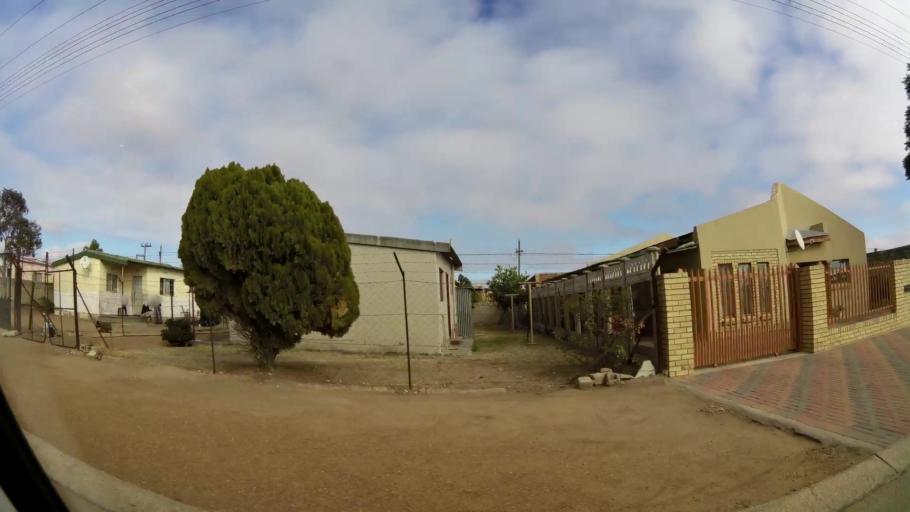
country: ZA
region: Limpopo
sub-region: Capricorn District Municipality
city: Polokwane
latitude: -23.8444
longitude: 29.3826
